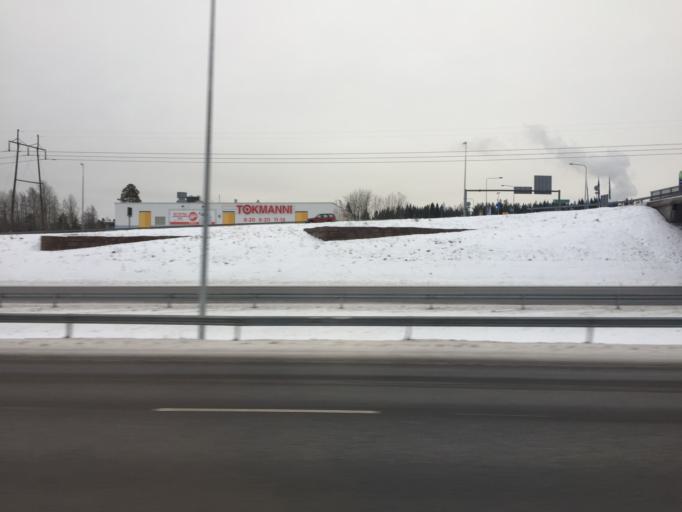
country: FI
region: Uusimaa
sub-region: Loviisa
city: Lovisa
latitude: 60.4610
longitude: 26.1932
